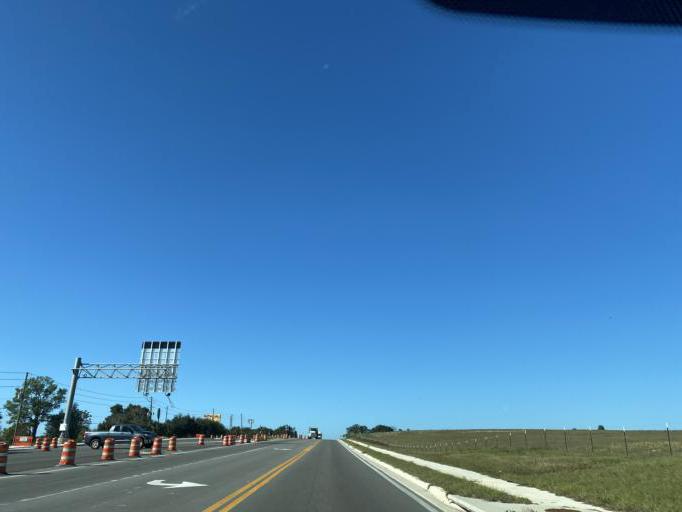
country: US
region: Florida
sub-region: Lake County
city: Mount Dora
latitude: 28.8010
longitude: -81.5934
